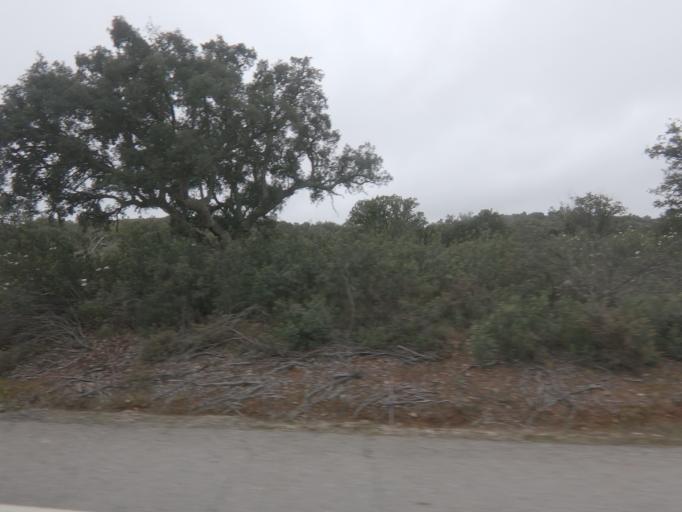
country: ES
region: Extremadura
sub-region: Provincia de Badajoz
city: Puebla de Obando
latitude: 39.2778
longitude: -6.5204
